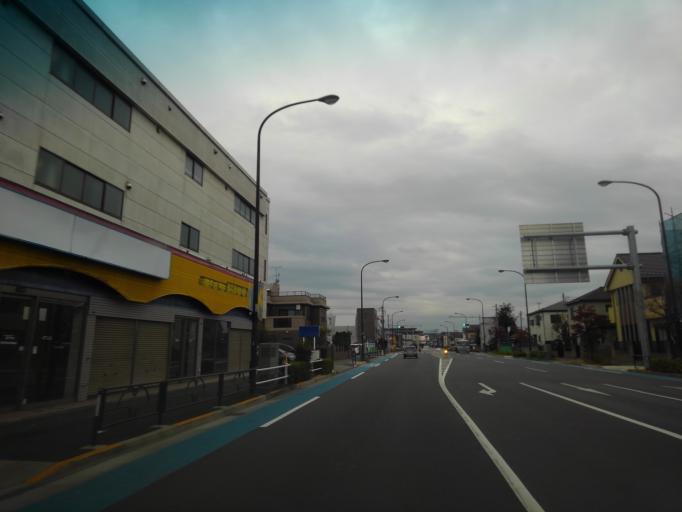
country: JP
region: Tokyo
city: Chofugaoka
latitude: 35.6545
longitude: 139.5388
